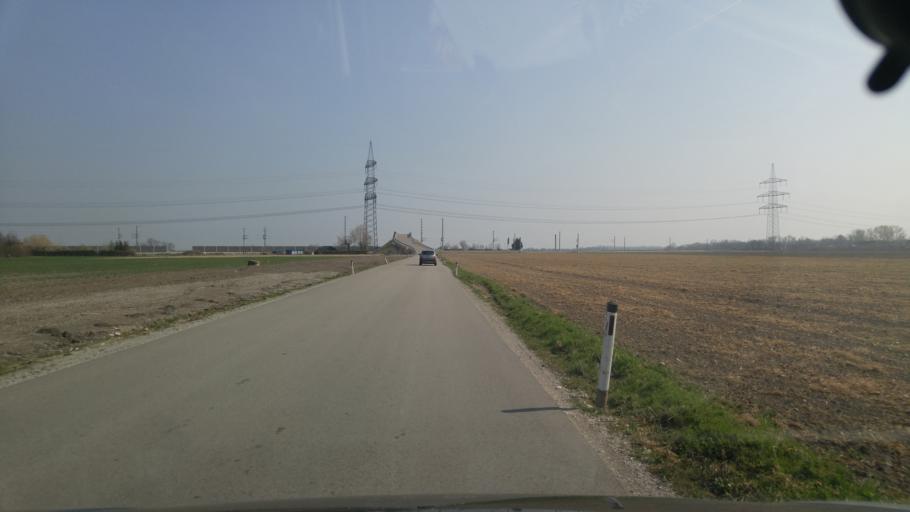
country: AT
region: Lower Austria
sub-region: Politischer Bezirk Modling
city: Munchendorf
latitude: 48.0206
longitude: 16.3841
